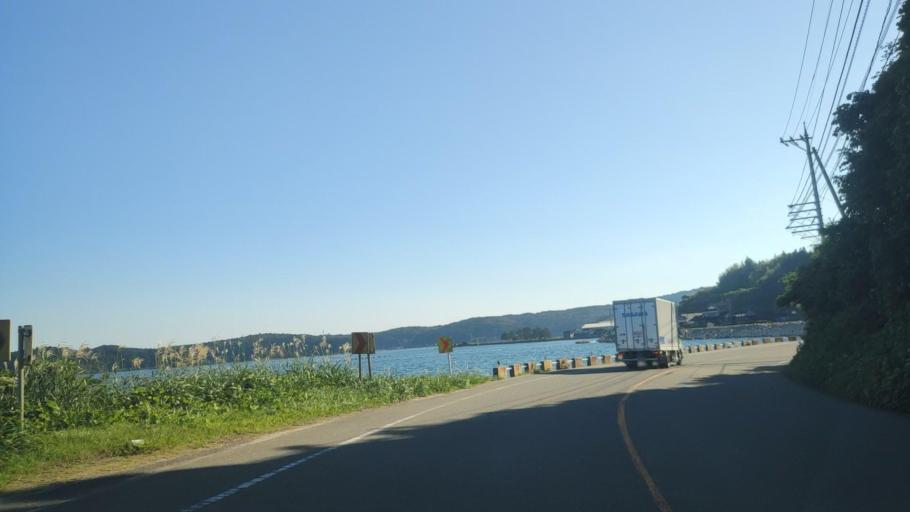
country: JP
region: Ishikawa
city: Nanao
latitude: 37.1546
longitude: 136.8808
